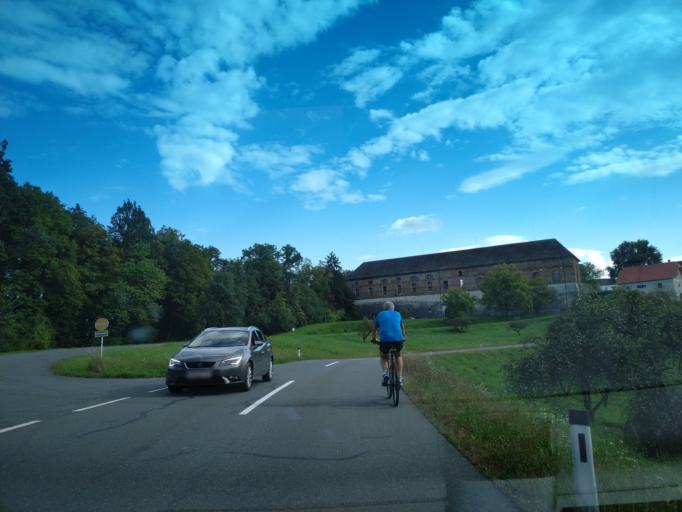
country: AT
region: Styria
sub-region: Politischer Bezirk Leibnitz
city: Leibnitz
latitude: 46.7848
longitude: 15.5238
